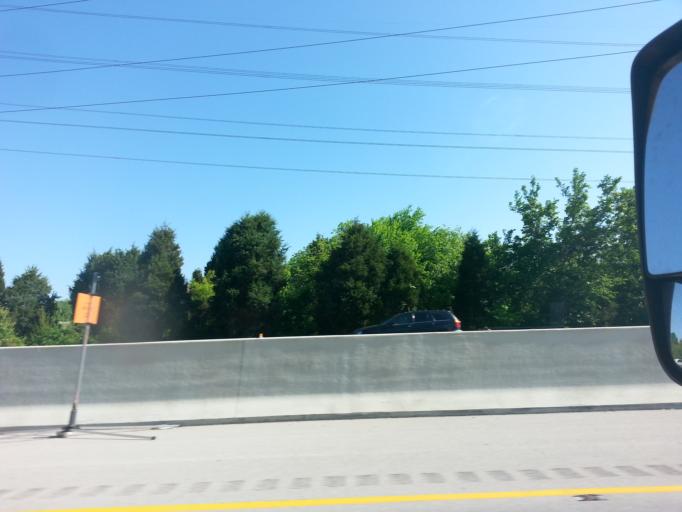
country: US
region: Kentucky
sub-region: Jefferson County
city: Middletown
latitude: 38.2222
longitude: -85.4930
